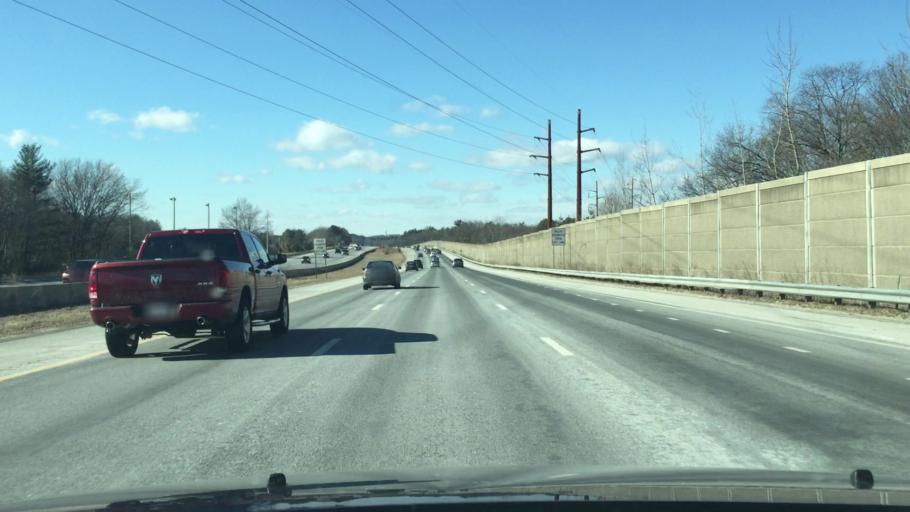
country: US
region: Massachusetts
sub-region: Middlesex County
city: Chelmsford
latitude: 42.6241
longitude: -71.3731
